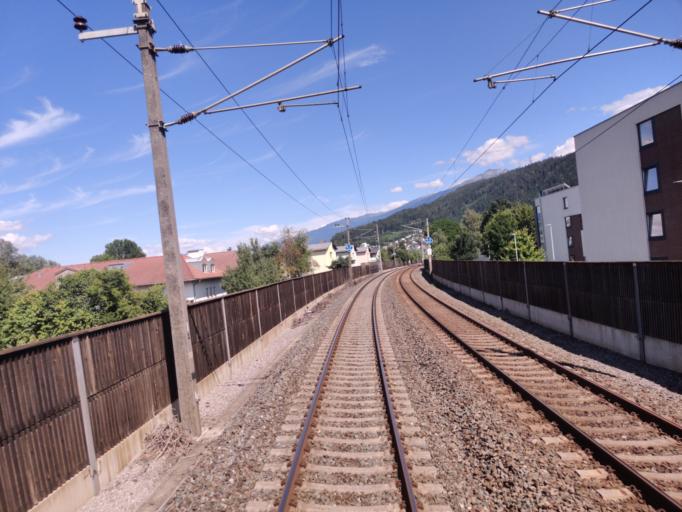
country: AT
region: Tyrol
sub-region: Politischer Bezirk Innsbruck Land
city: Vols
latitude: 47.2532
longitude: 11.3536
